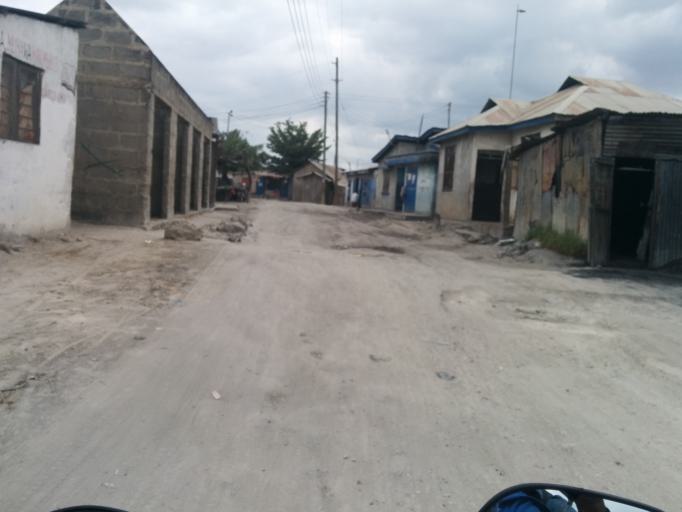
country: TZ
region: Dar es Salaam
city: Dar es Salaam
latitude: -6.8688
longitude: 39.2441
